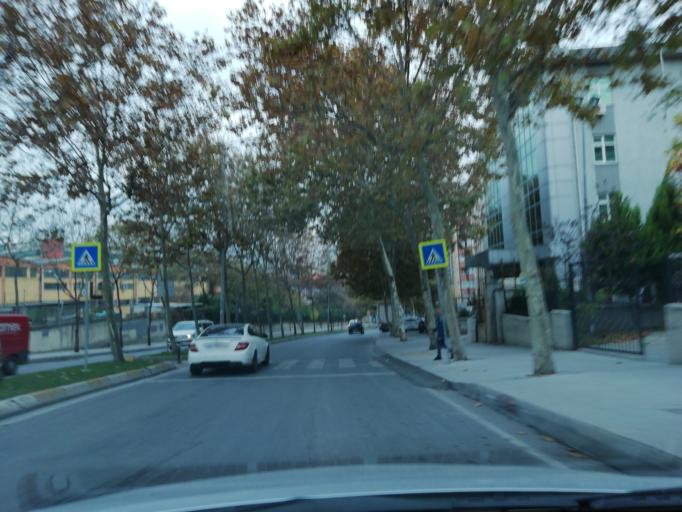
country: TR
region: Istanbul
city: Mahmutbey
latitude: 41.0222
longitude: 28.8238
